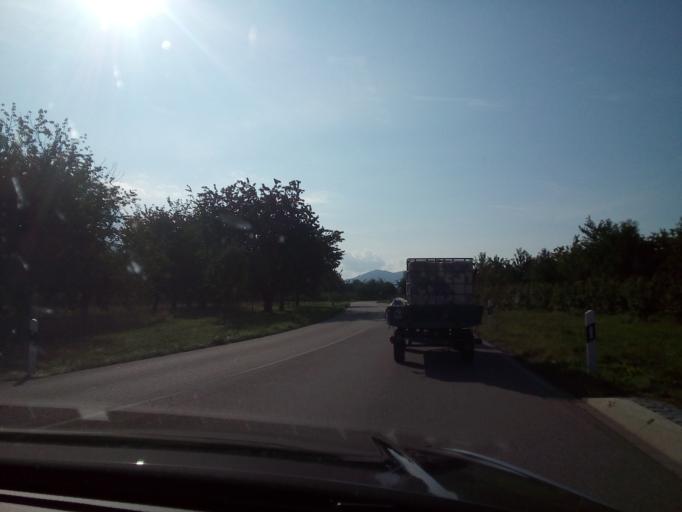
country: DE
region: Baden-Wuerttemberg
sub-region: Freiburg Region
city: Haslach
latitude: 48.5570
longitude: 8.0492
